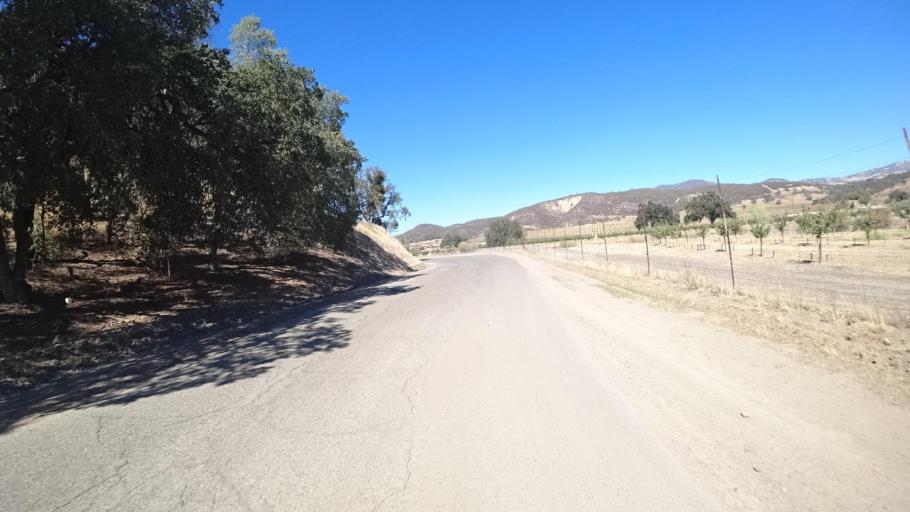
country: US
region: California
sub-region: Fresno County
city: Coalinga
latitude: 35.9223
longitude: -120.4423
